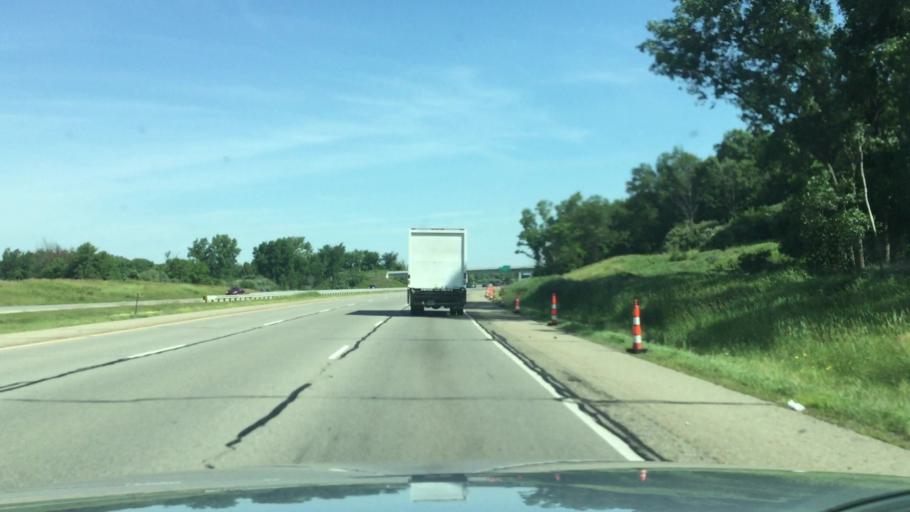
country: US
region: Michigan
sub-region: Oakland County
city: Holly
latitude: 42.8544
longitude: -83.5907
